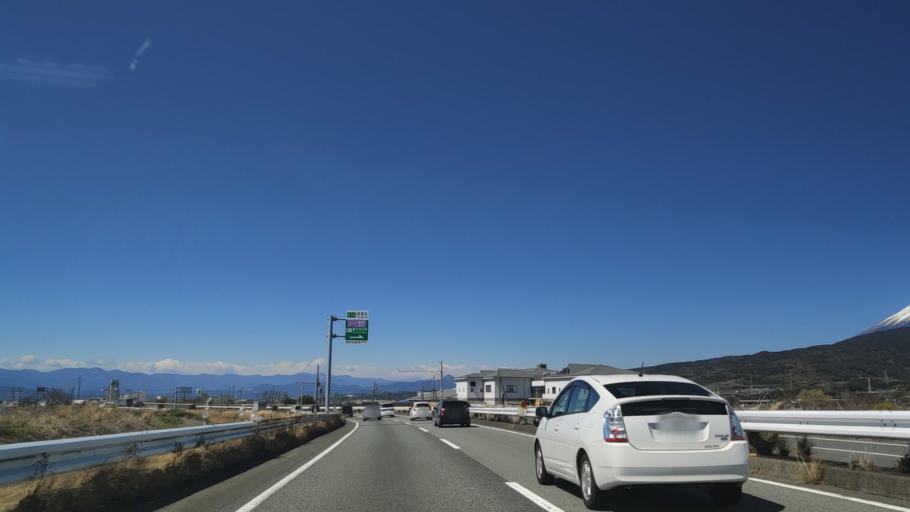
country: JP
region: Shizuoka
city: Numazu
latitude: 35.1333
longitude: 138.7860
